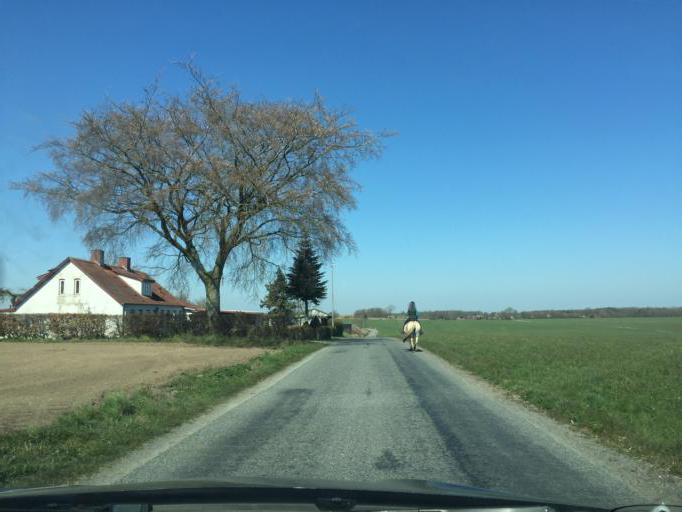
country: DK
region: South Denmark
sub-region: Faaborg-Midtfyn Kommune
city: Arslev
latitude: 55.2881
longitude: 10.5293
